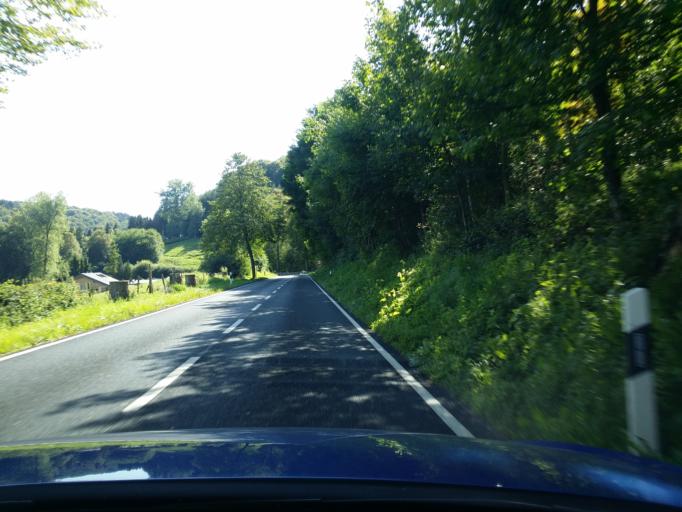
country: LU
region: Luxembourg
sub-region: Canton de Capellen
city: Kopstal
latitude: 49.6768
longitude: 6.0818
